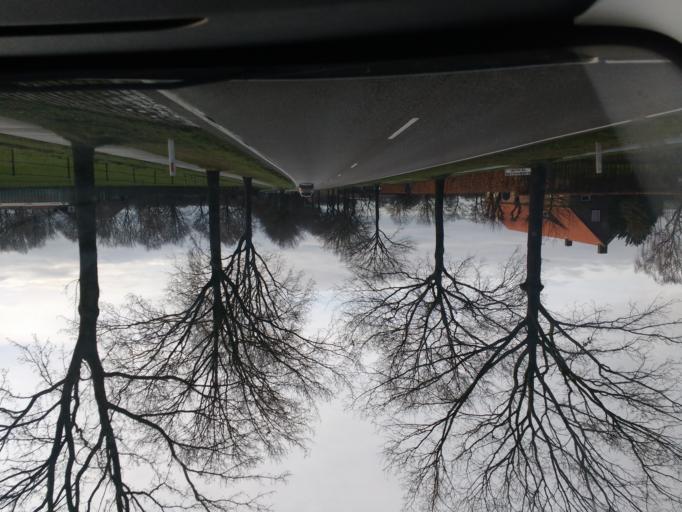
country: NL
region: North Brabant
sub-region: Gemeente Boxmeer
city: Overloon
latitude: 51.4889
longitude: 5.8525
